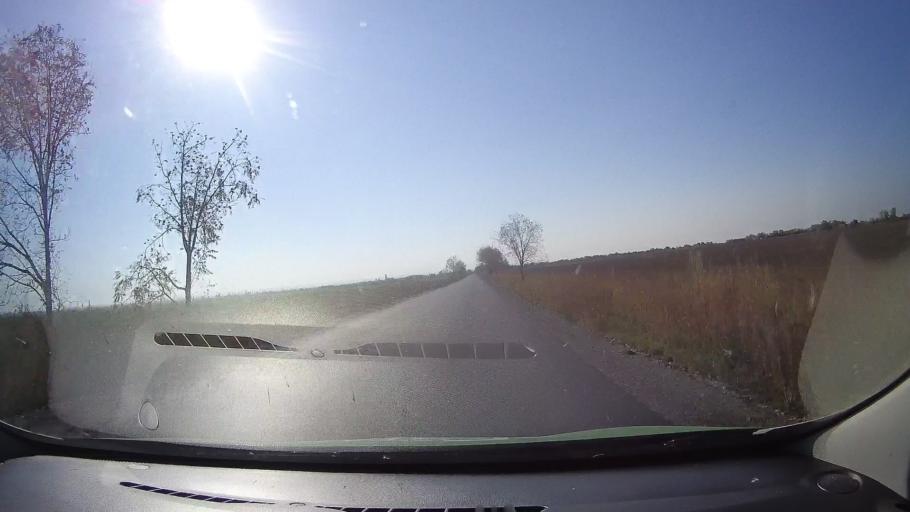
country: RO
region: Satu Mare
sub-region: Comuna Tiream
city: Tiream
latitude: 47.6285
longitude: 22.4675
